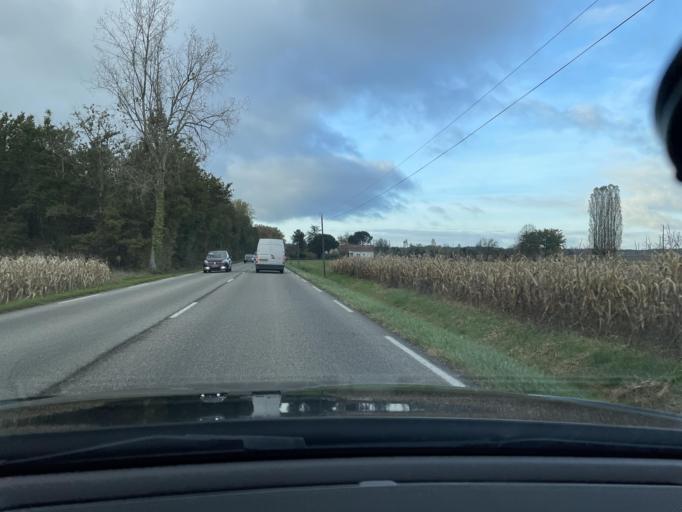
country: FR
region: Aquitaine
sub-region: Departement du Lot-et-Garonne
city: Casteljaloux
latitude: 44.3701
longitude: 0.1067
